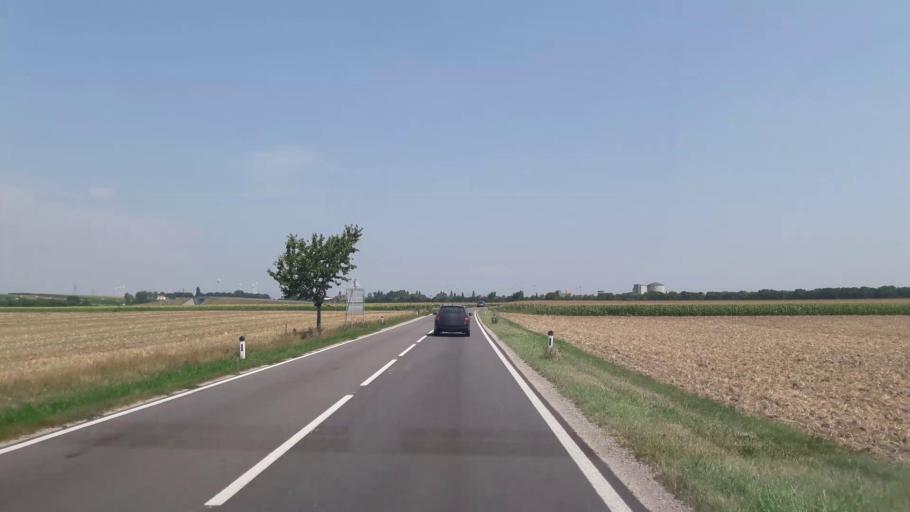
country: AT
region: Lower Austria
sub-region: Politischer Bezirk Bruck an der Leitha
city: Bruck an der Leitha
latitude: 48.0145
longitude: 16.7343
